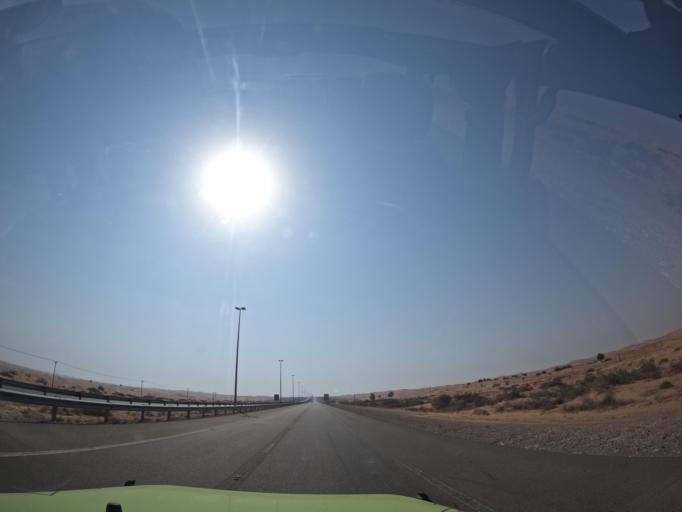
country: OM
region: Al Buraimi
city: Al Buraymi
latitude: 24.4561
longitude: 55.6457
